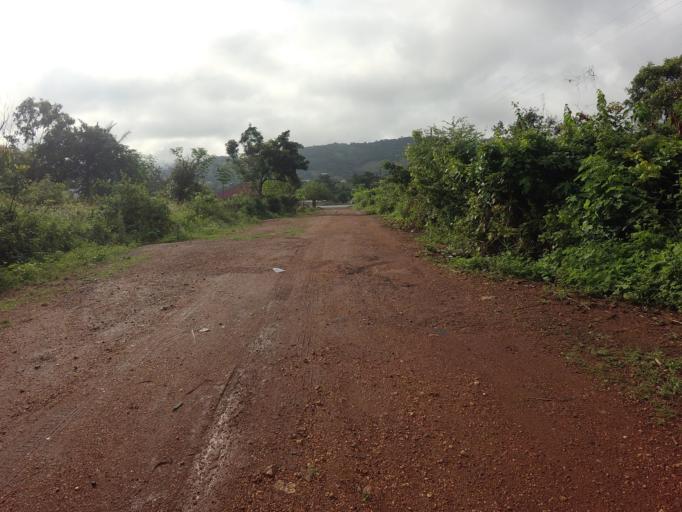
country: GH
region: Volta
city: Ho
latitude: 6.5347
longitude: 0.2294
